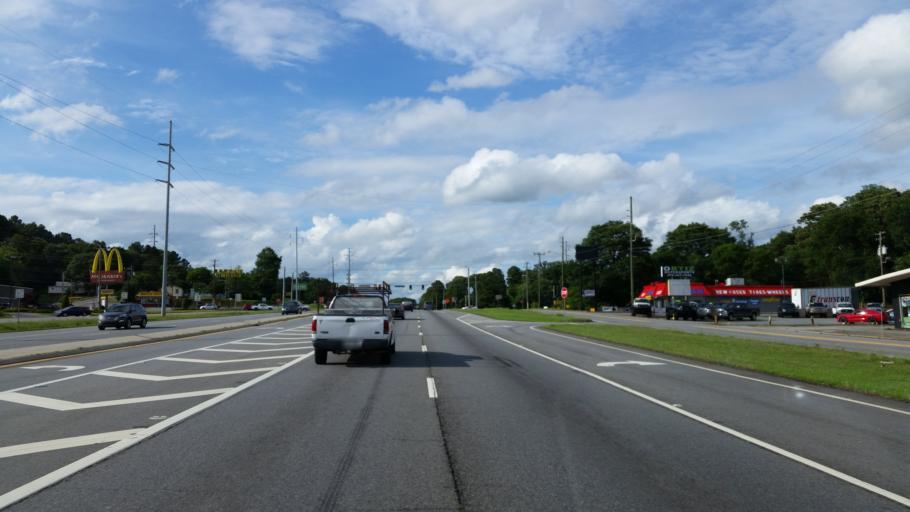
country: US
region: Georgia
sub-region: Bartow County
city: Cartersville
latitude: 34.1748
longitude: -84.7864
